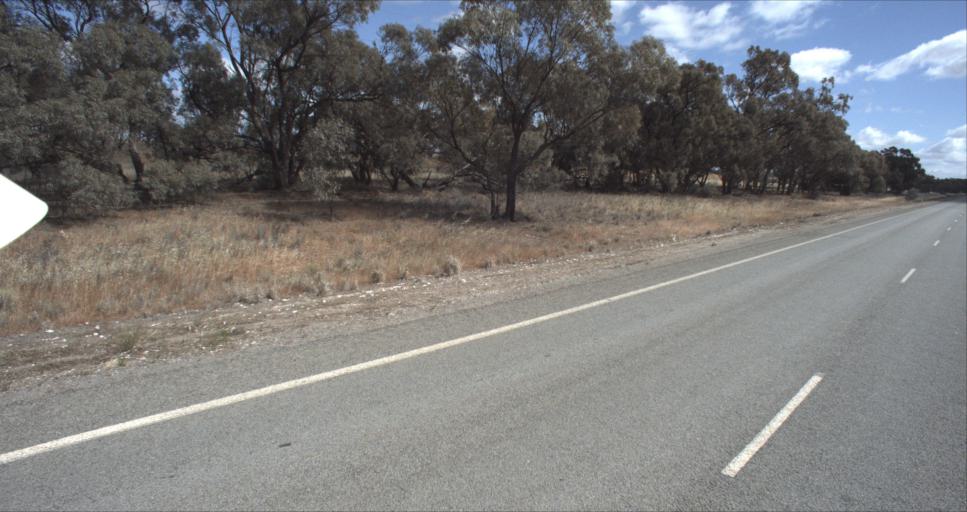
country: AU
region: New South Wales
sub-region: Murrumbidgee Shire
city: Darlington Point
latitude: -34.5731
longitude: 146.1668
